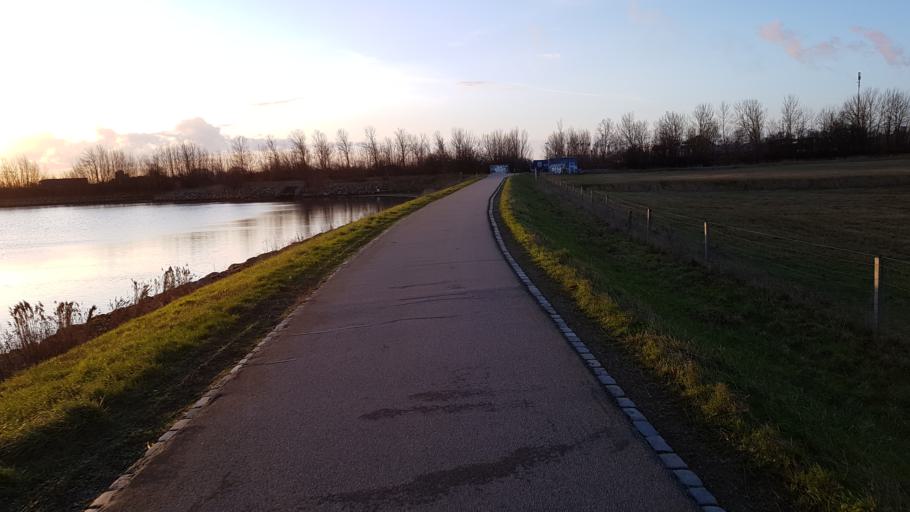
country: DK
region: Capital Region
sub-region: Hvidovre Kommune
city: Hvidovre
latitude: 55.6169
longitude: 12.4979
